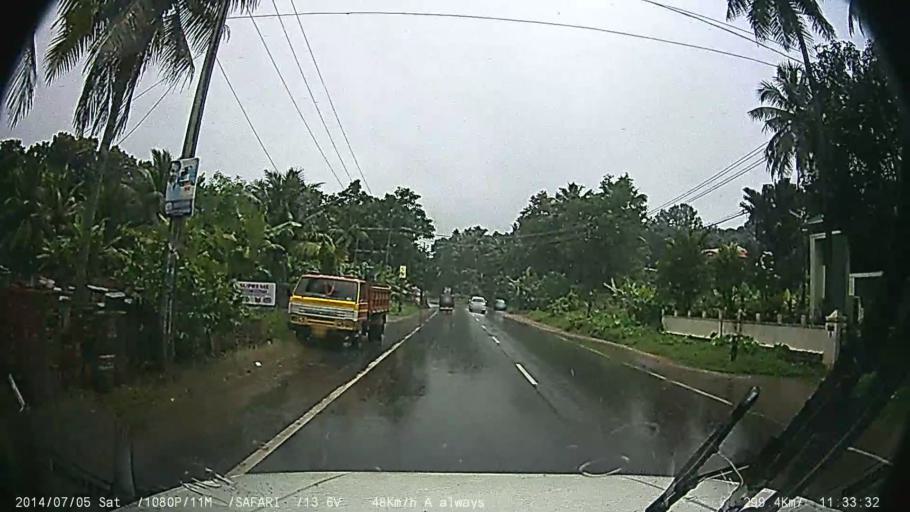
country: IN
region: Kerala
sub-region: Ernakulam
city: Muvattupula
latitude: 9.9733
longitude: 76.6009
